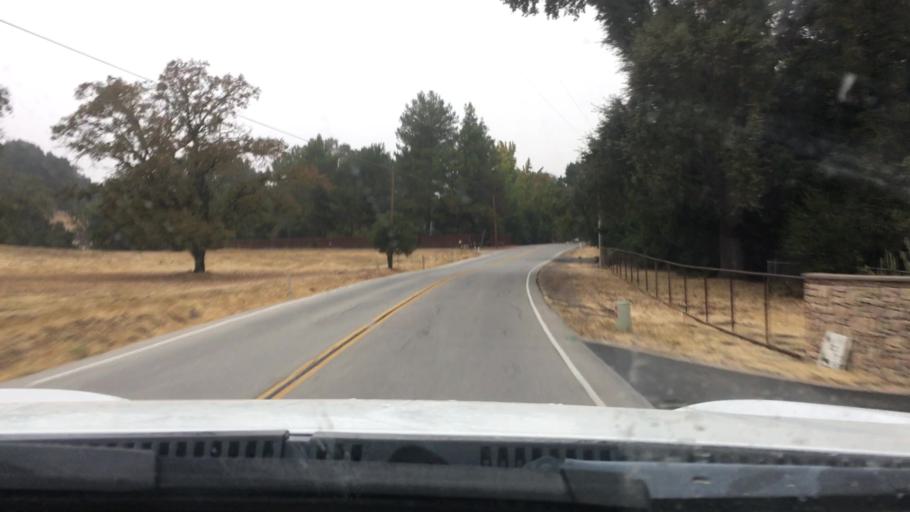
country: US
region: California
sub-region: San Luis Obispo County
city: Atascadero
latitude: 35.4928
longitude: -120.6847
